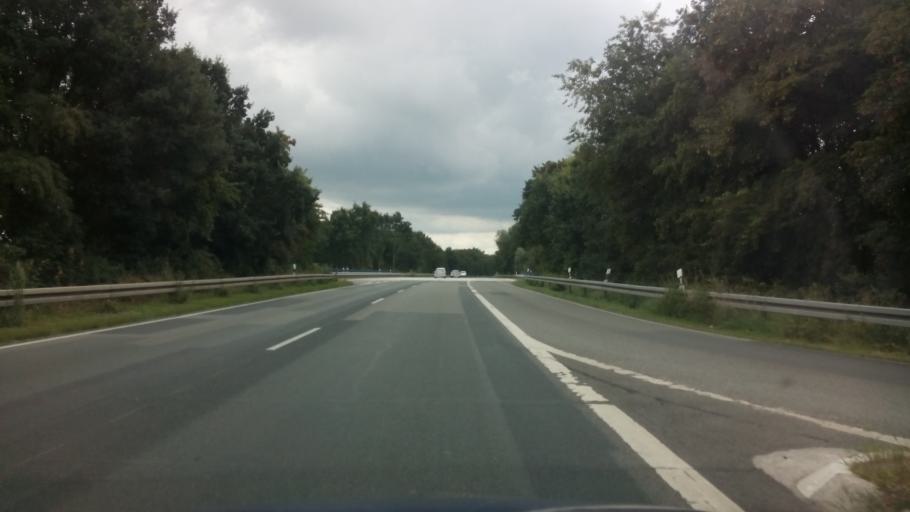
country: DE
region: Lower Saxony
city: Diepholz
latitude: 52.6082
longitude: 8.3589
